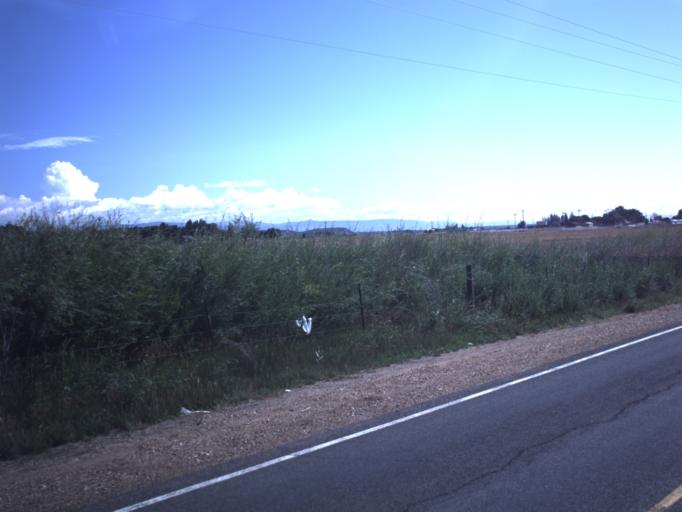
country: US
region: Utah
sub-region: Duchesne County
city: Duchesne
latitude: 40.3592
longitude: -110.2986
